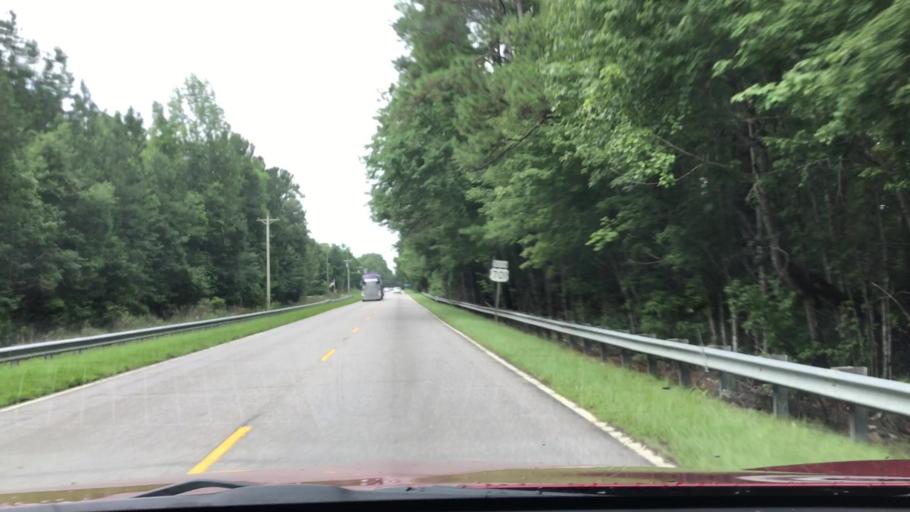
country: US
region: South Carolina
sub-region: Georgetown County
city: Murrells Inlet
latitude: 33.5642
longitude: -79.2133
